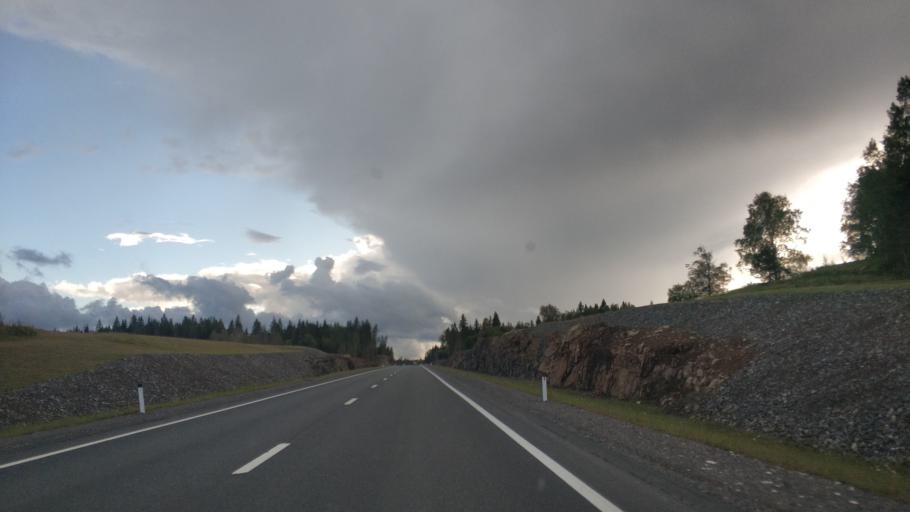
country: RU
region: Republic of Karelia
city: Lakhdenpokh'ya
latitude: 61.4370
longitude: 29.9800
